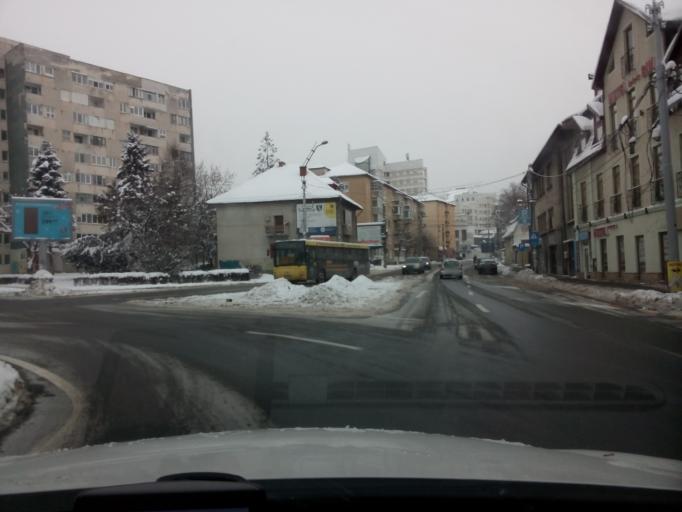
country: RO
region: Sibiu
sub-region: Municipiul Sibiu
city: Sibiu
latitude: 45.7894
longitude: 24.1498
